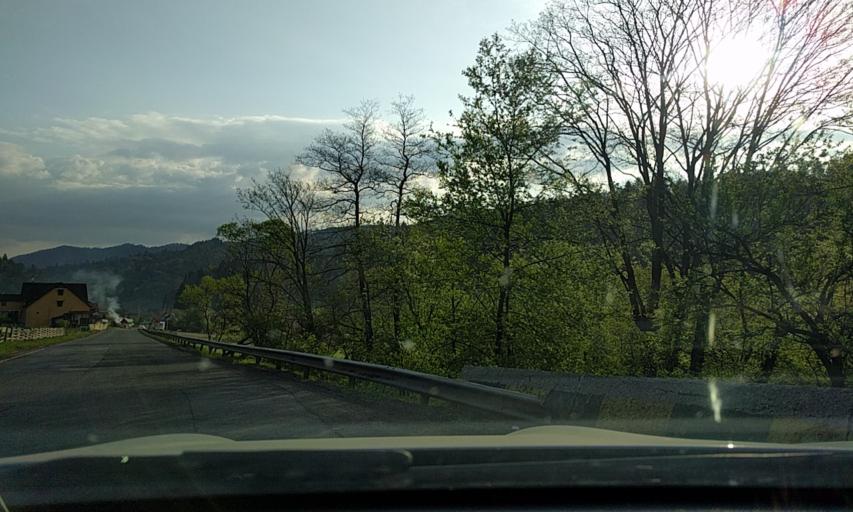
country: RO
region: Covasna
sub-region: Comuna Bretcu
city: Bretcu
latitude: 46.0671
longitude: 26.3840
